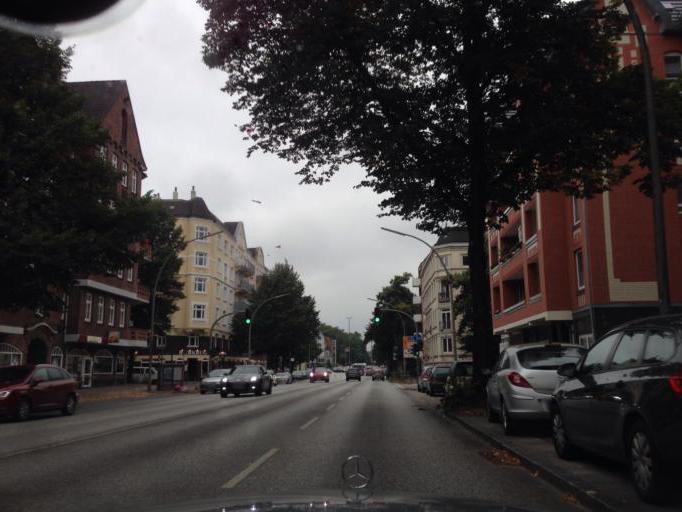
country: DE
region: Hamburg
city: Hamburg-Nord
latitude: 53.5938
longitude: 9.9840
